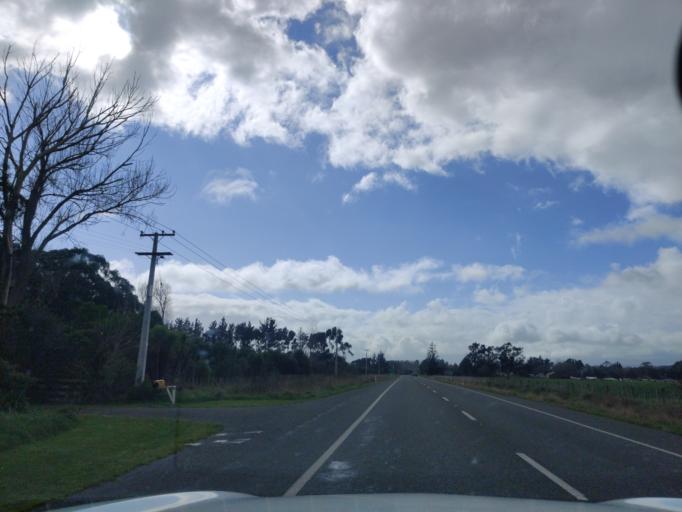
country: NZ
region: Manawatu-Wanganui
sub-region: Palmerston North City
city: Palmerston North
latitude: -40.4215
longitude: 175.5884
